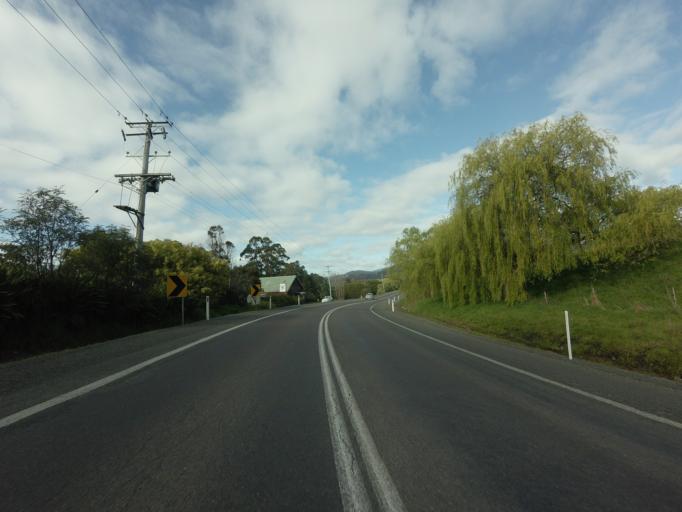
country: AU
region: Tasmania
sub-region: Huon Valley
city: Franklin
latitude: -43.1291
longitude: 146.9900
